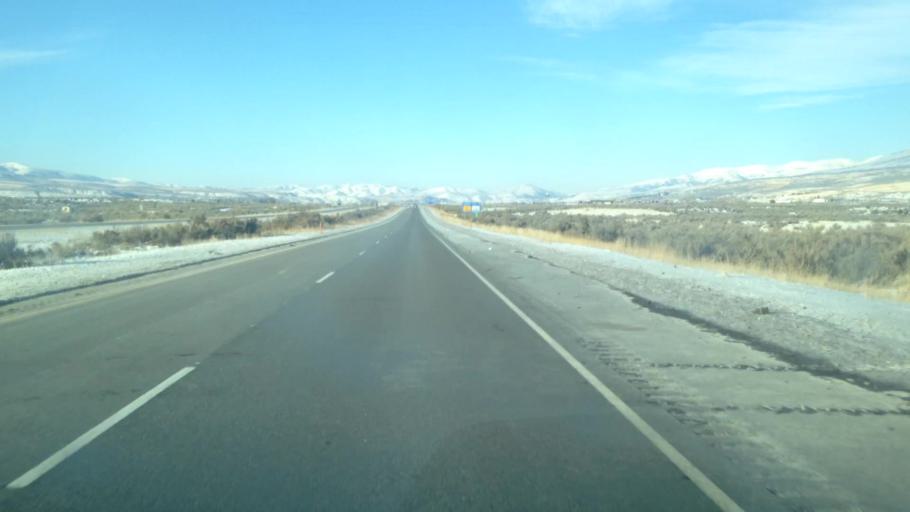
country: US
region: Idaho
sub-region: Bannock County
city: Pocatello
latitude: 42.6430
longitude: -112.2063
